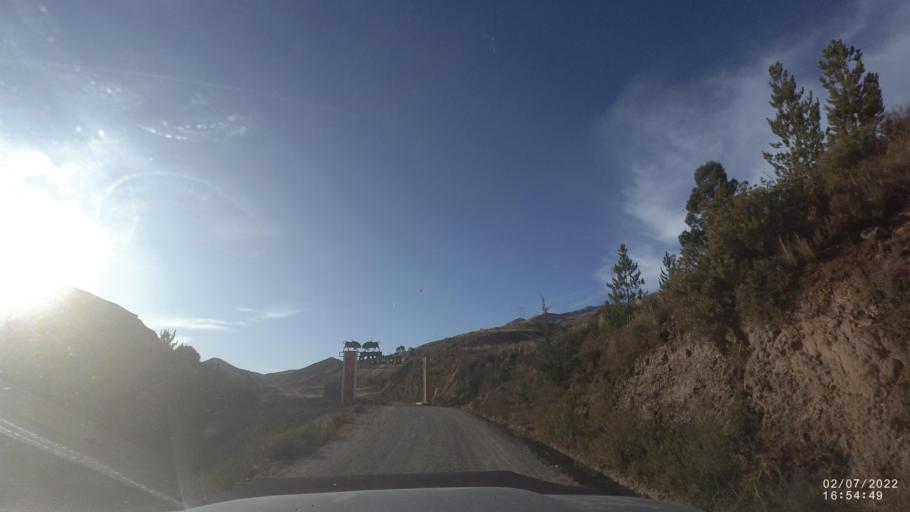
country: BO
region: Cochabamba
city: Irpa Irpa
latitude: -17.9642
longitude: -66.5399
